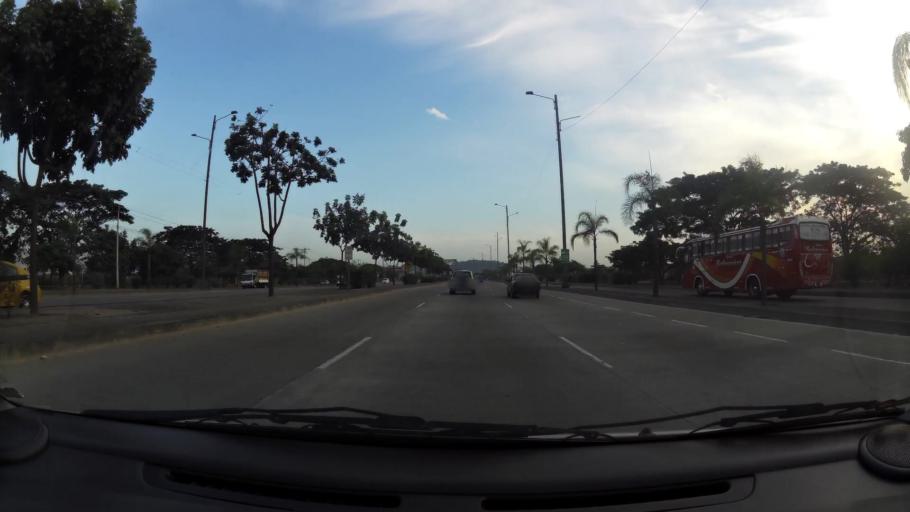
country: EC
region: Guayas
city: Eloy Alfaro
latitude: -2.0932
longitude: -79.8936
